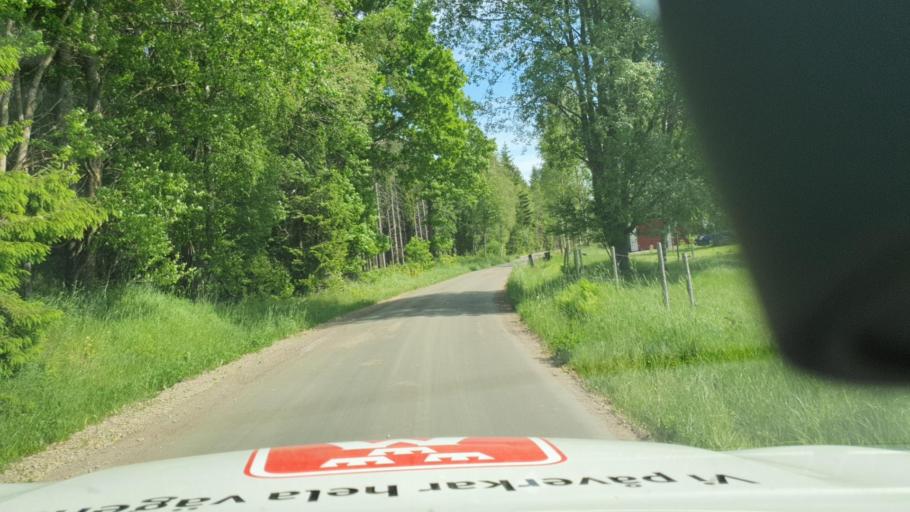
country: SE
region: Vaestra Goetaland
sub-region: Herrljunga Kommun
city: Herrljunga
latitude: 57.9431
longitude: 12.9863
